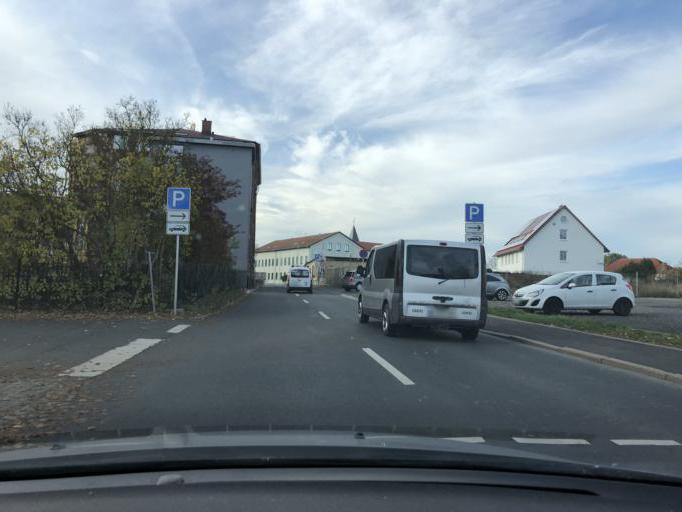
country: DE
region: Thuringia
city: Hildburghausen
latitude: 50.4271
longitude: 10.7331
